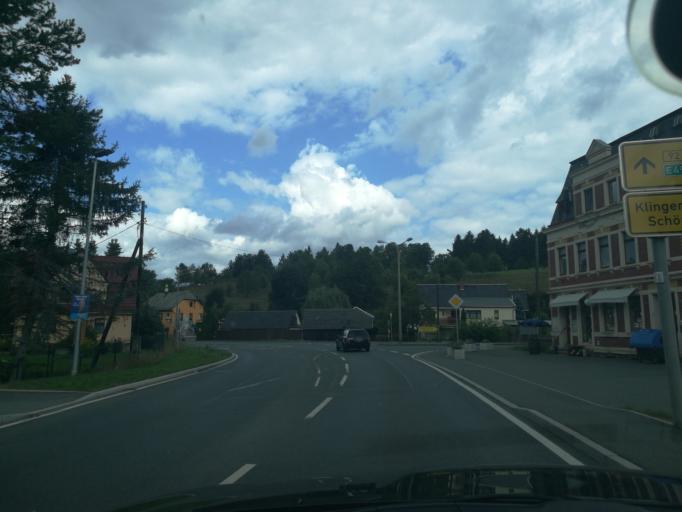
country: DE
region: Saxony
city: Oelsnitz
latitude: 50.4009
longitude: 12.1851
